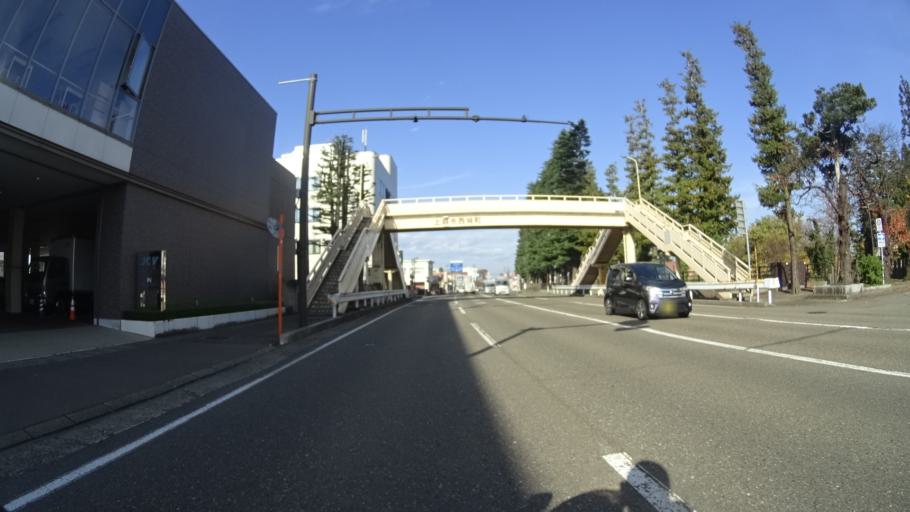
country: JP
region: Niigata
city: Joetsu
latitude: 37.1129
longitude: 138.2507
